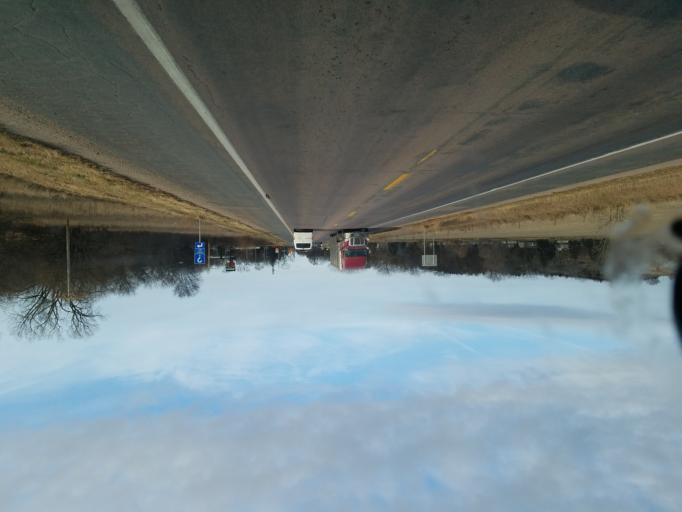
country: US
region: South Dakota
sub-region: Union County
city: Dakota Dunes
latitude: 42.4482
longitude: -96.5745
